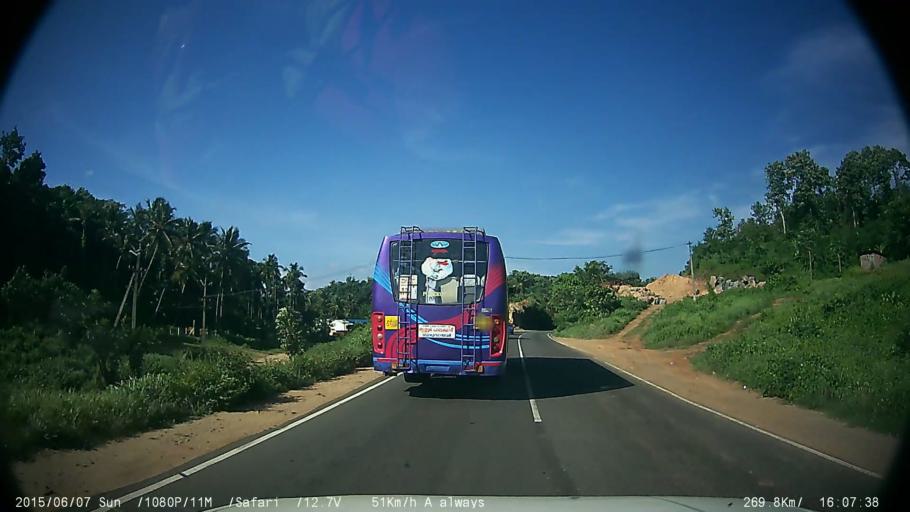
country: IN
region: Kerala
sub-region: Thrissur District
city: Chelakara
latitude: 10.5911
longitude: 76.4595
